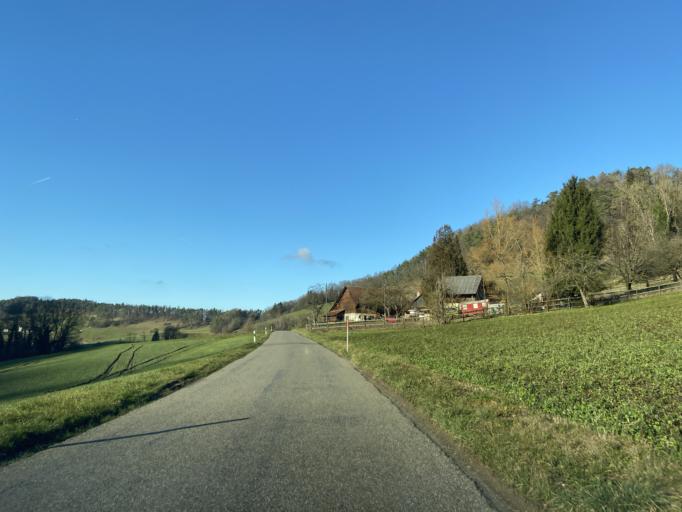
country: CH
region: Zurich
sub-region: Bezirk Winterthur
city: Wuelflingen (Kreis 6) / Niederfeld
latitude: 47.5027
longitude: 8.6615
